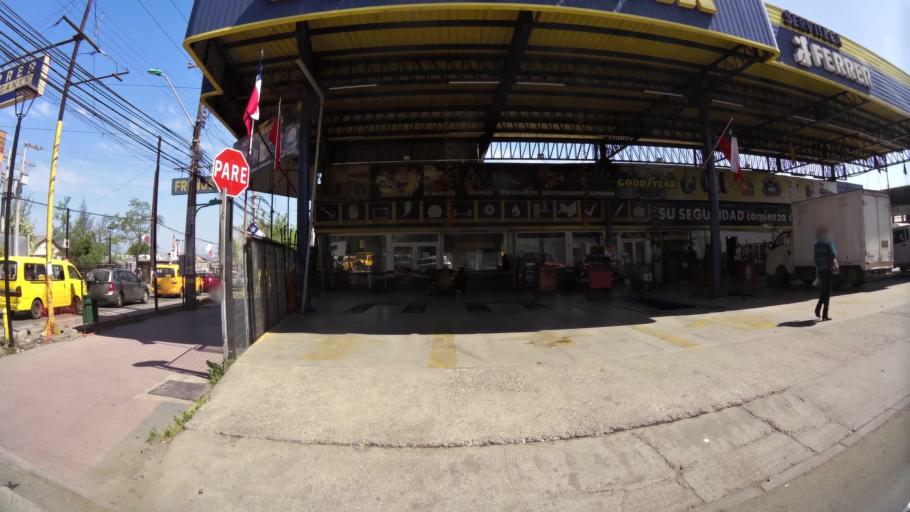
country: CL
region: Santiago Metropolitan
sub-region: Provincia de Talagante
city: Talagante
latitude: -33.6598
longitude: -70.9187
